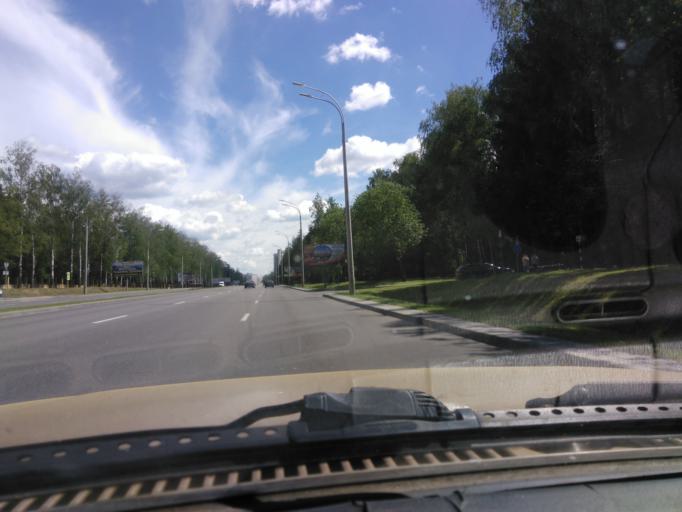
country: BY
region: Mogilev
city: Mahilyow
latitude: 53.9249
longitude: 30.2754
